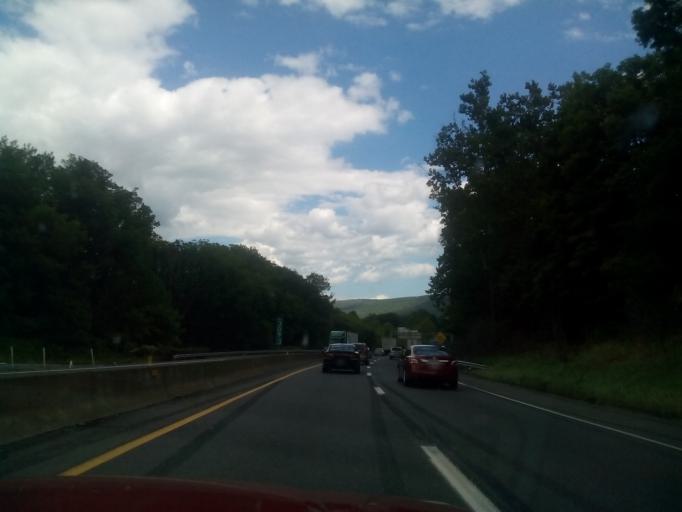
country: US
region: Pennsylvania
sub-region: Monroe County
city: East Stroudsburg
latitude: 40.9985
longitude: -75.1535
